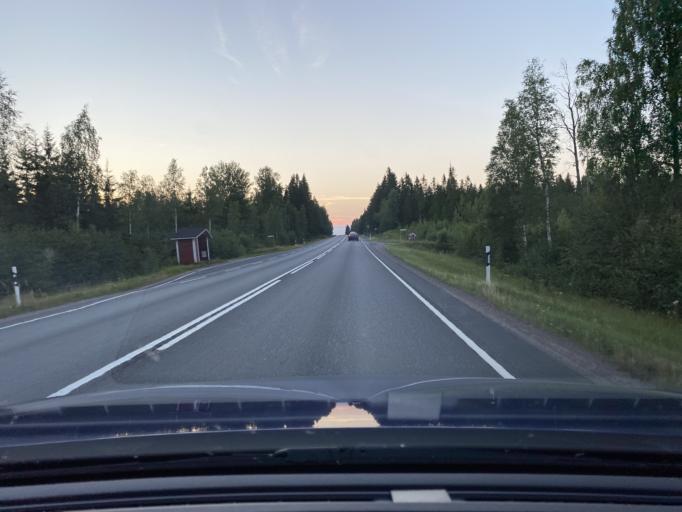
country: FI
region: Pirkanmaa
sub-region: Luoteis-Pirkanmaa
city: Ikaalinen
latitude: 61.8340
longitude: 22.9402
